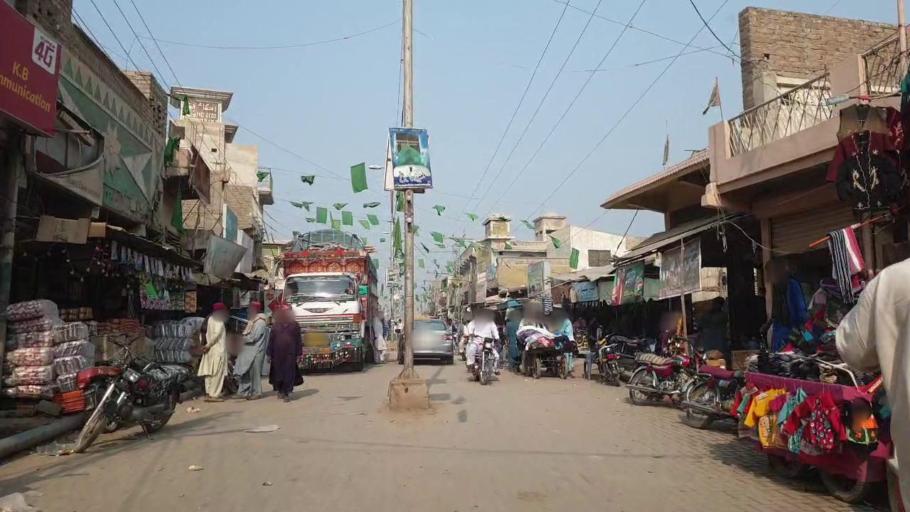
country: PK
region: Sindh
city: Bhan
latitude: 26.5585
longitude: 67.7209
